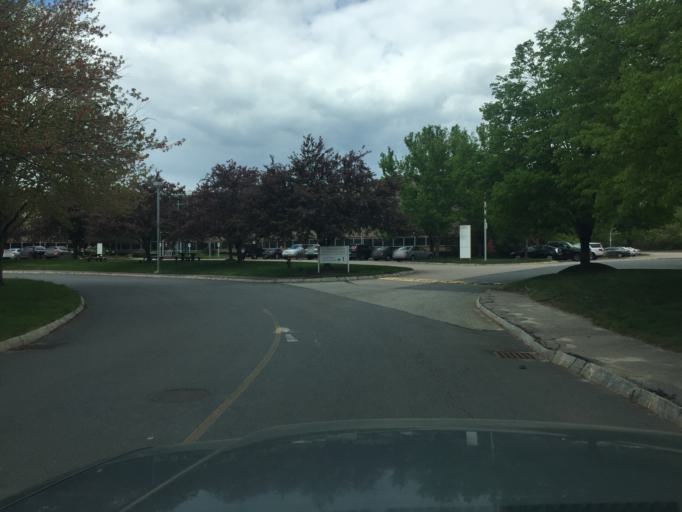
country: US
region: Massachusetts
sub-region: Norfolk County
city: Norwood
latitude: 42.1615
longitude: -71.2023
